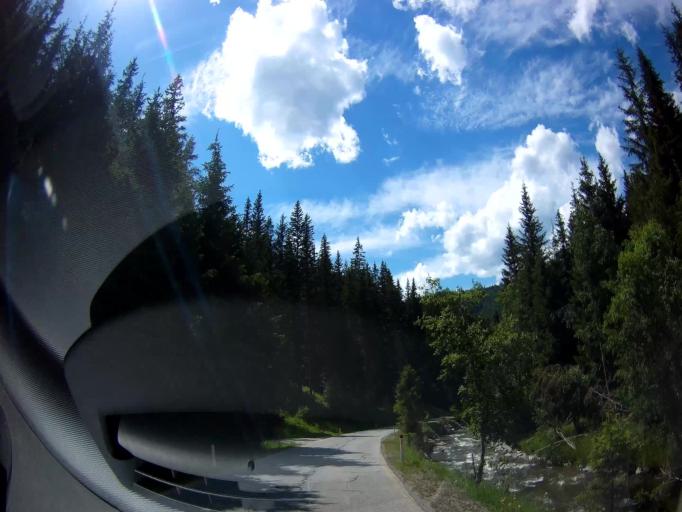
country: AT
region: Styria
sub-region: Politischer Bezirk Murau
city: Stadl an der Mur
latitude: 47.0134
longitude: 14.0075
